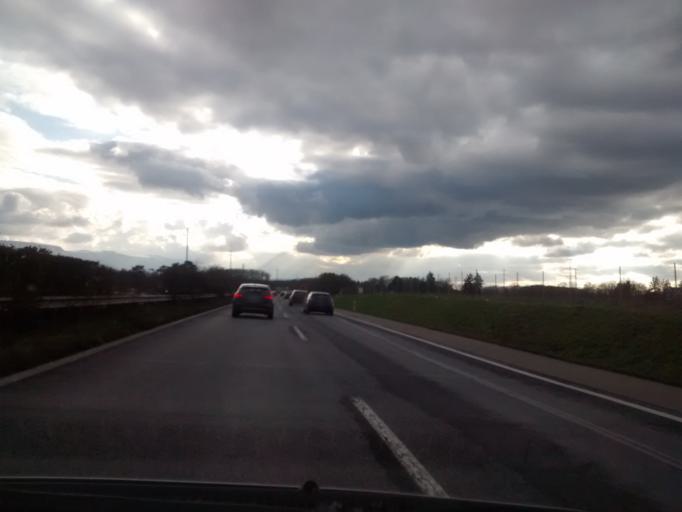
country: CH
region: Geneva
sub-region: Geneva
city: Versoix
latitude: 46.2863
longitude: 6.1453
